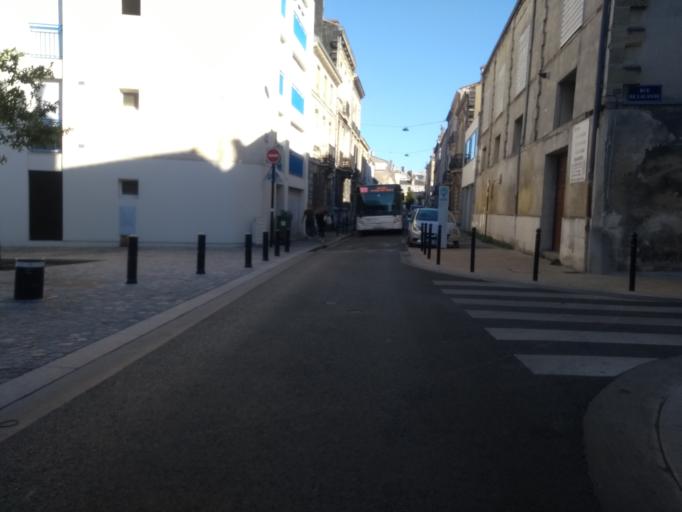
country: FR
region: Aquitaine
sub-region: Departement de la Gironde
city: Bordeaux
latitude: 44.8320
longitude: -0.5754
